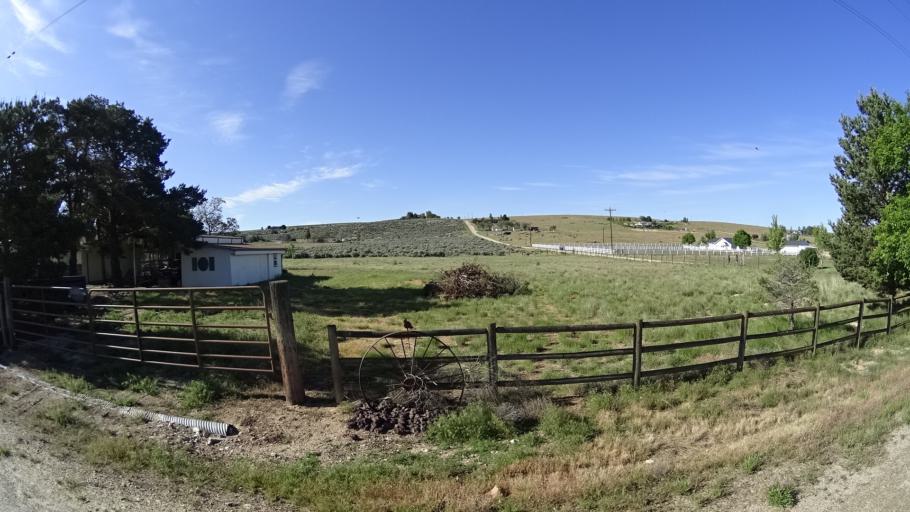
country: US
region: Idaho
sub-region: Ada County
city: Garden City
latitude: 43.5247
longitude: -116.2865
